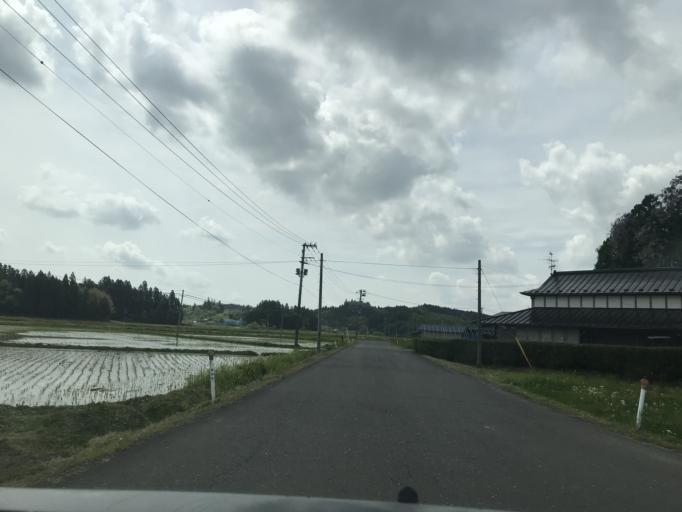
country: JP
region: Iwate
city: Ichinoseki
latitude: 38.8460
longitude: 141.0187
